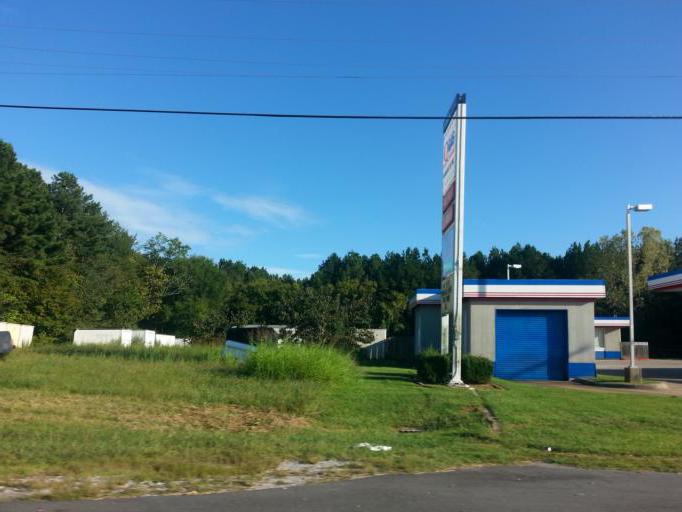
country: US
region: Alabama
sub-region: Lauderdale County
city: Killen
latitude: 34.8425
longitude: -87.5900
